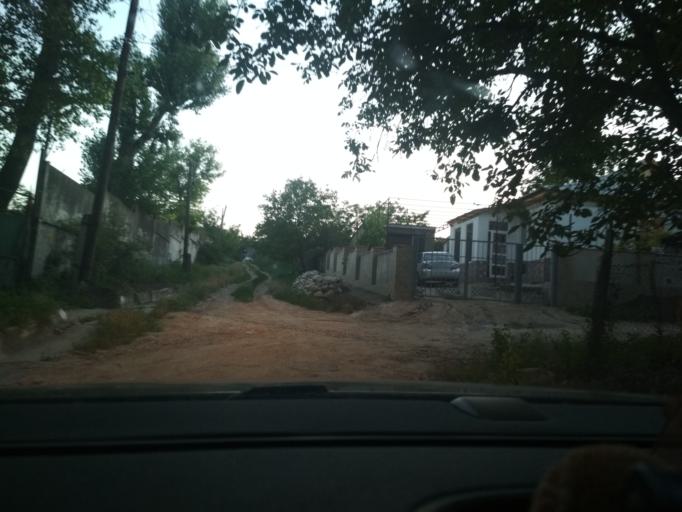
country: MD
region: Nisporeni
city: Nisporeni
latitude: 47.0751
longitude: 28.1740
